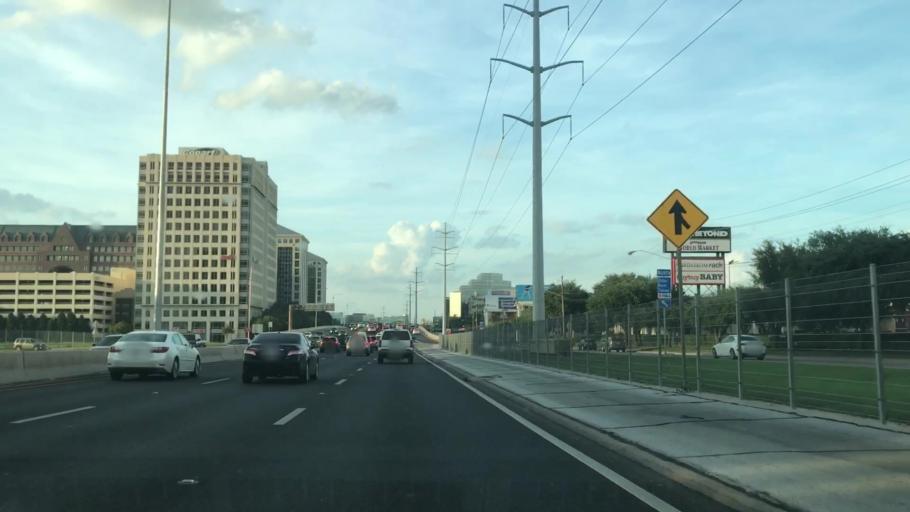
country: US
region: Texas
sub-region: Dallas County
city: Addison
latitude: 32.9363
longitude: -96.8220
